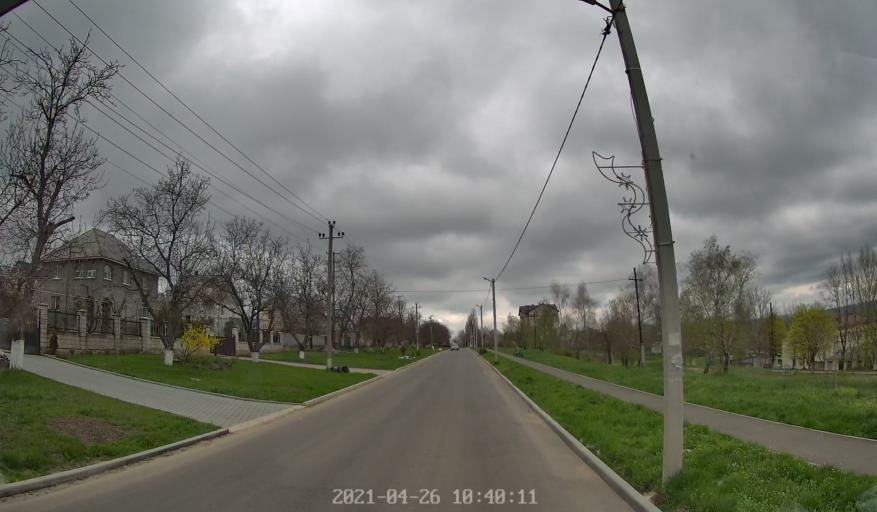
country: MD
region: Chisinau
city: Cricova
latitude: 47.1330
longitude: 28.8605
